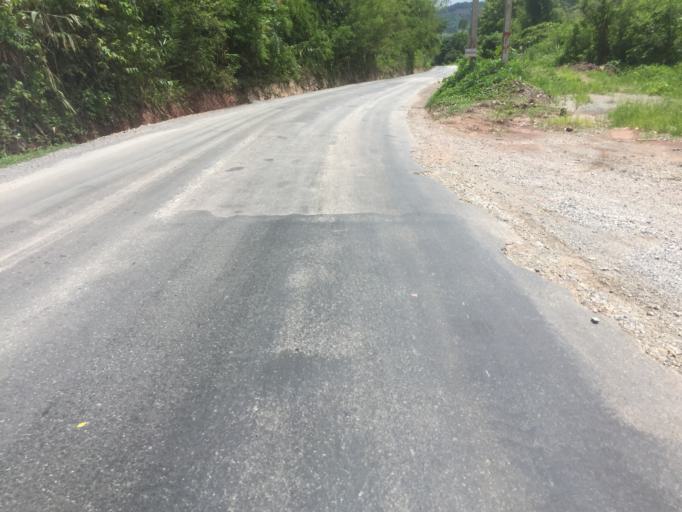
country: LA
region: Oudomxai
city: Muang Xay
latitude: 20.7420
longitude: 102.0283
